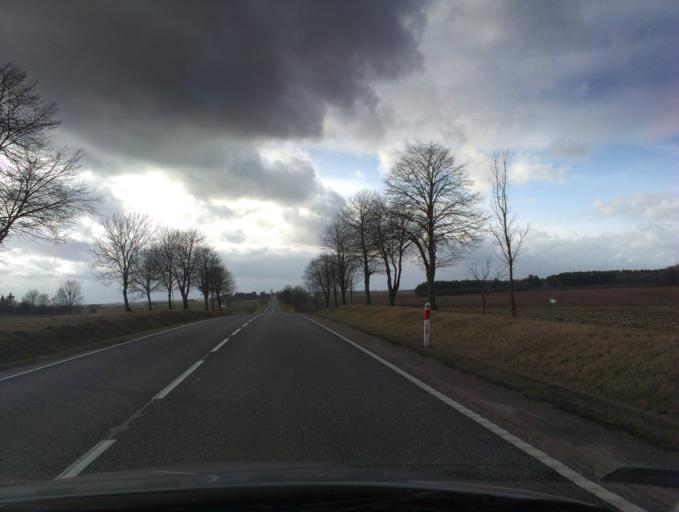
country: PL
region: Pomeranian Voivodeship
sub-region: Powiat czluchowski
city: Czluchow
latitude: 53.6347
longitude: 17.2784
